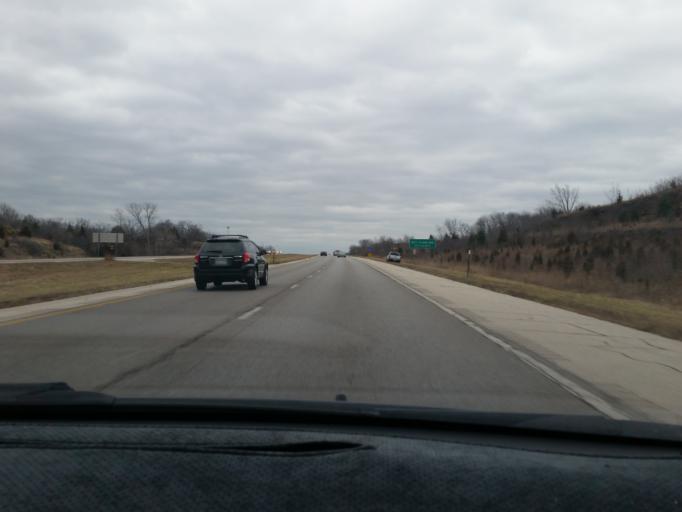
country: US
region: Kansas
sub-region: Johnson County
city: De Soto
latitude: 38.9601
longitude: -94.9686
